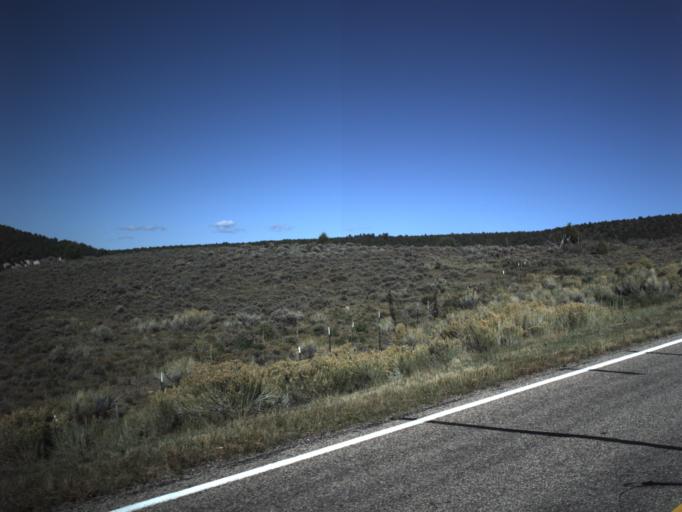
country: US
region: Utah
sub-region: Garfield County
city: Panguitch
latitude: 37.7674
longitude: -112.5443
